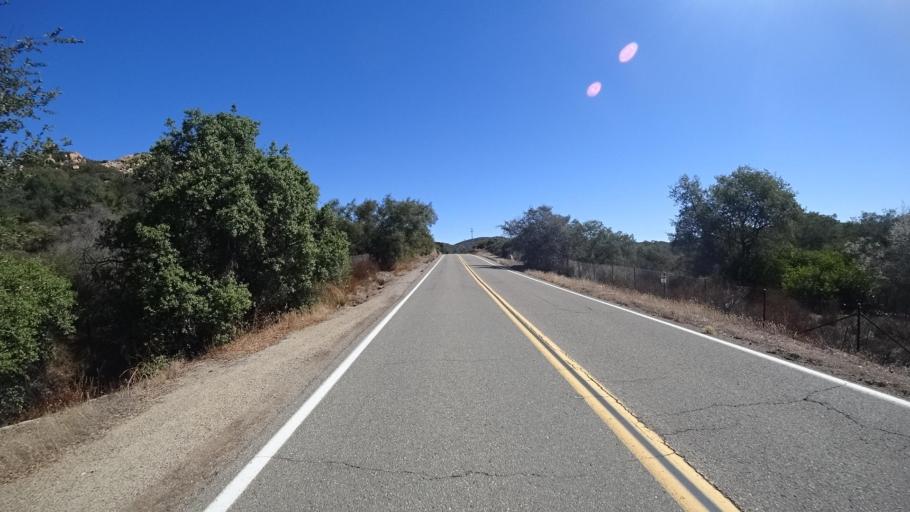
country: US
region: California
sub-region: San Diego County
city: Descanso
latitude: 32.8001
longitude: -116.6492
